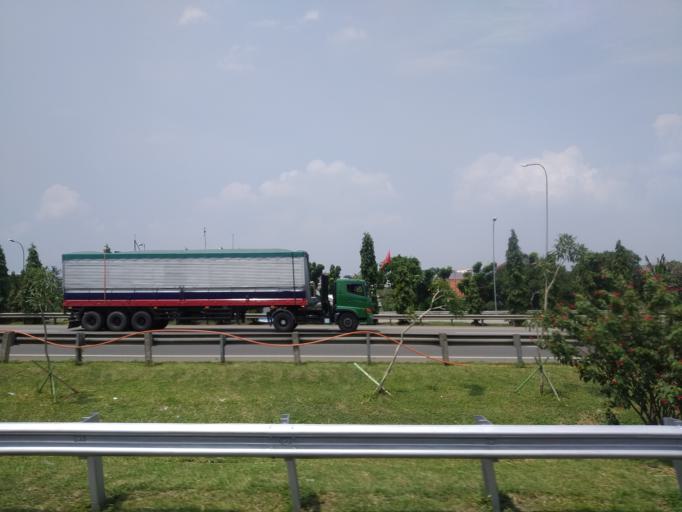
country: ID
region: West Java
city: Citeureup
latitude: -6.4836
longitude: 106.8736
